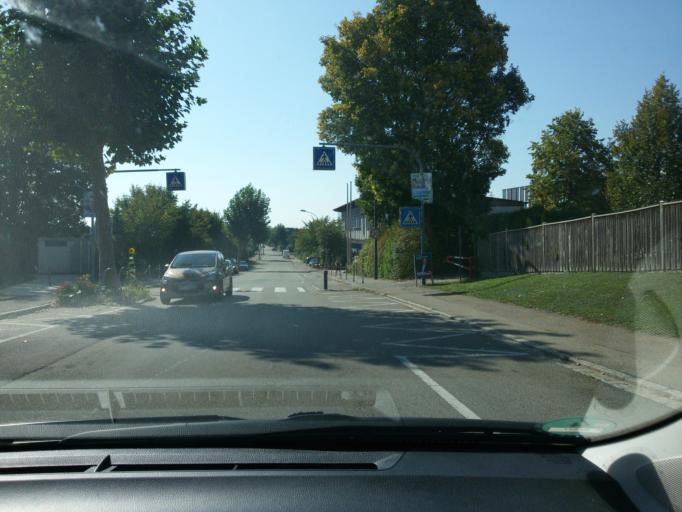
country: DE
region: Bavaria
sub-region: Swabia
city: Oettingen in Bayern
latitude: 48.9535
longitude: 10.5984
